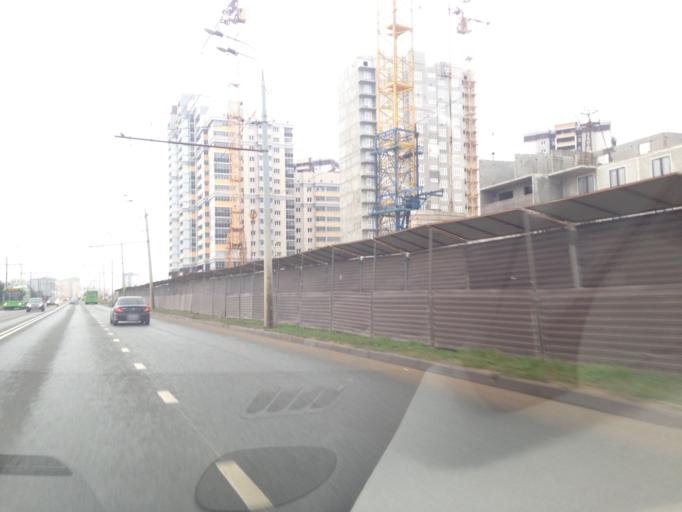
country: RU
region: Tatarstan
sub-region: Gorod Kazan'
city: Kazan
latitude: 55.7852
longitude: 49.1933
